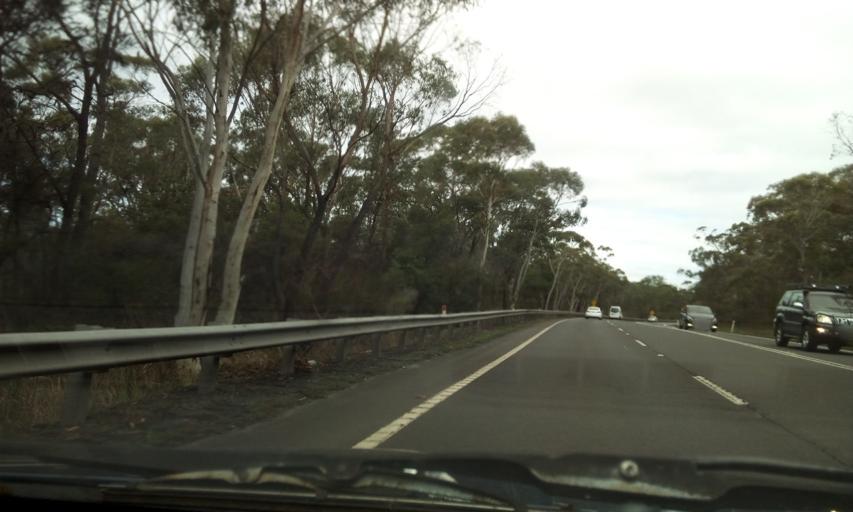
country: AU
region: New South Wales
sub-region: Wollondilly
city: Douglas Park
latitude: -34.2196
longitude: 150.8070
